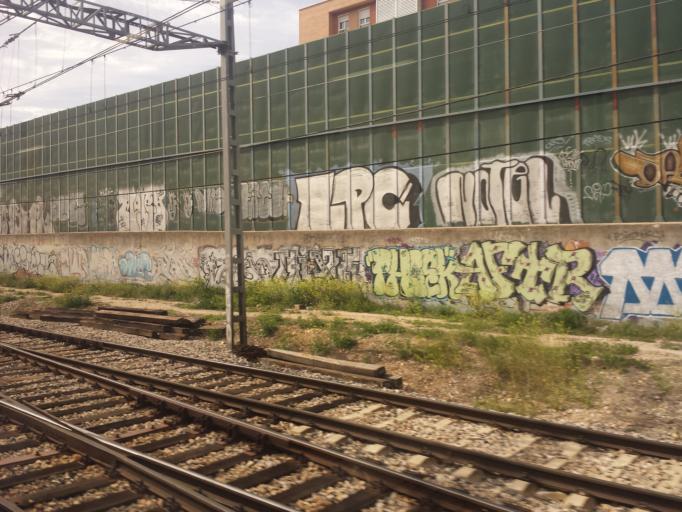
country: ES
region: Madrid
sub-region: Provincia de Madrid
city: Torrejon de Ardoz
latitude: 40.4559
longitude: -3.4739
